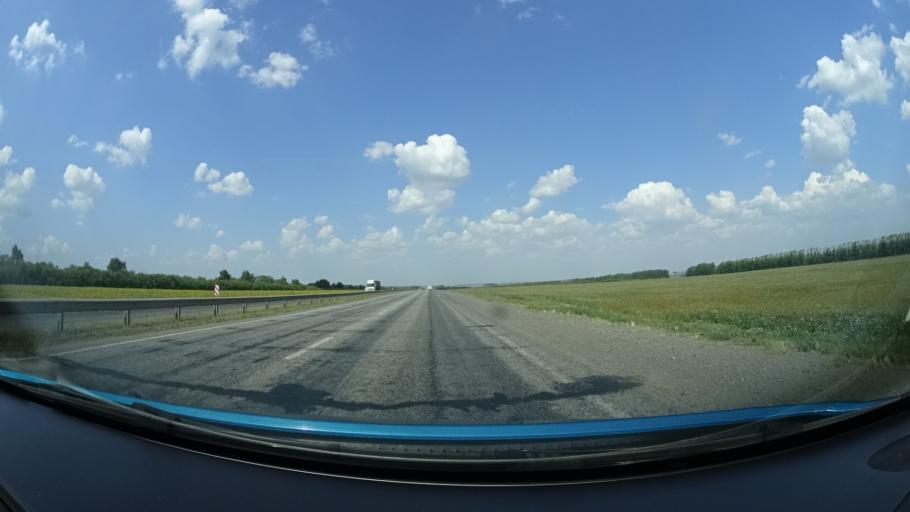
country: RU
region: Bashkortostan
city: Dmitriyevka
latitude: 54.7068
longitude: 55.2330
